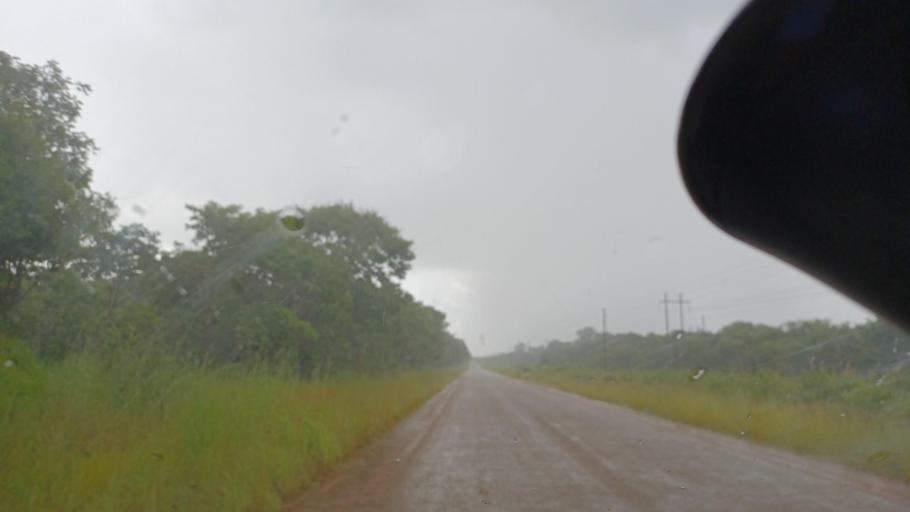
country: ZM
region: North-Western
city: Kasempa
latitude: -13.0908
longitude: 25.9428
